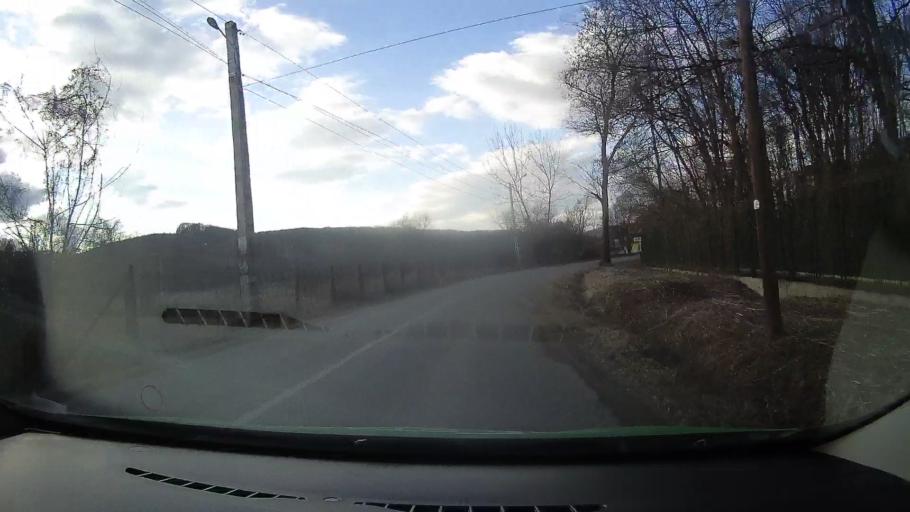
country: RO
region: Dambovita
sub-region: Comuna Gura Ocnitei
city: Gura Ocnitei
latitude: 44.9569
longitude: 25.5514
